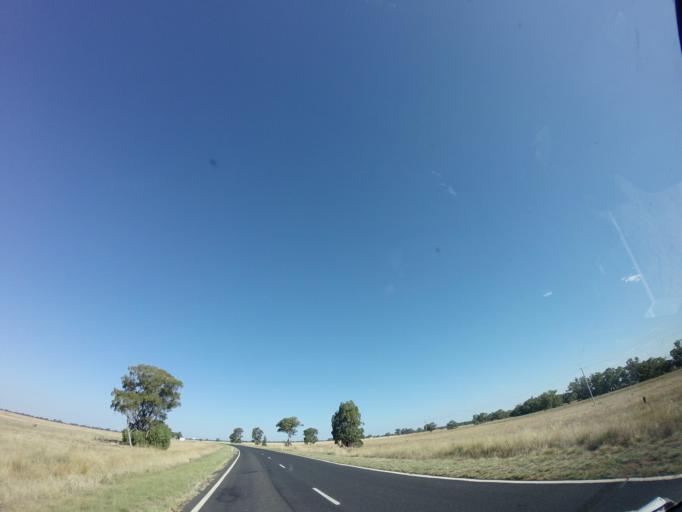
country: AU
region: New South Wales
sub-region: Gilgandra
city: Gilgandra
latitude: -31.7007
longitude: 148.5758
